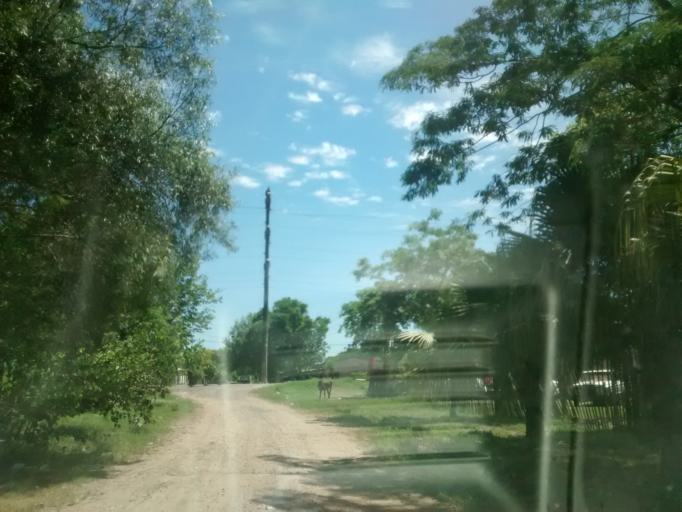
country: AR
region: Chaco
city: Resistencia
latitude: -27.4248
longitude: -58.9722
